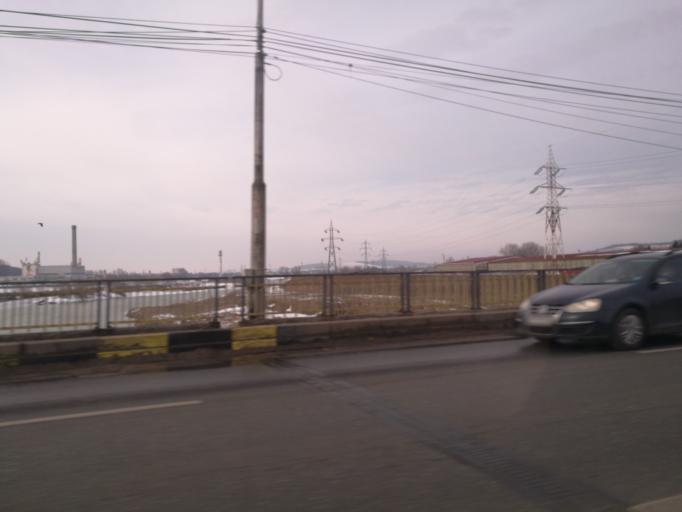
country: RO
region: Suceava
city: Suceava
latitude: 47.6587
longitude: 26.2642
